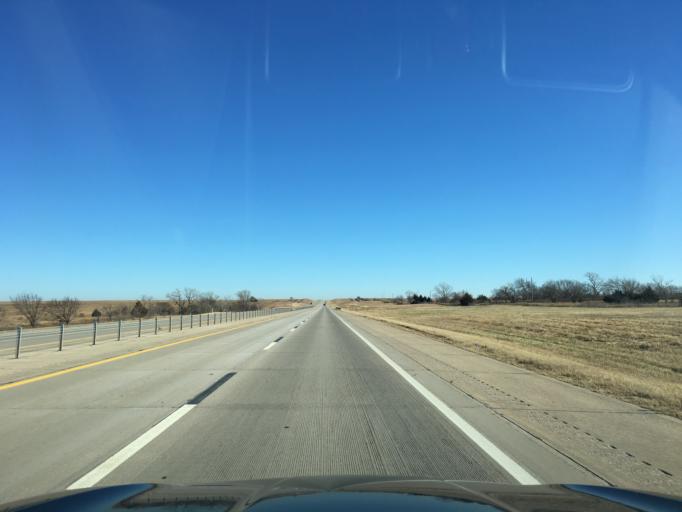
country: US
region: Oklahoma
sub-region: Noble County
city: Perry
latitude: 36.3920
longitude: -97.1683
